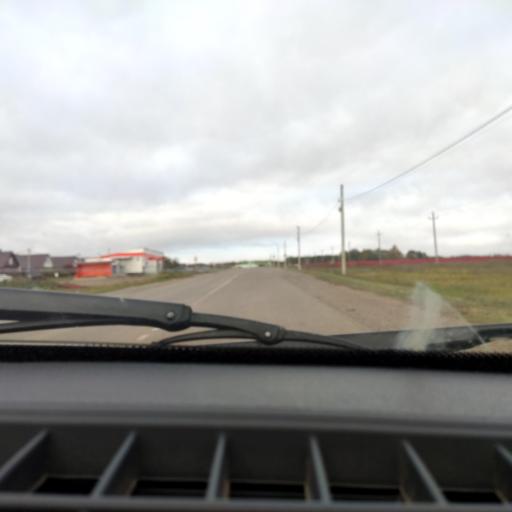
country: RU
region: Bashkortostan
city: Avdon
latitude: 54.6587
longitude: 55.7435
